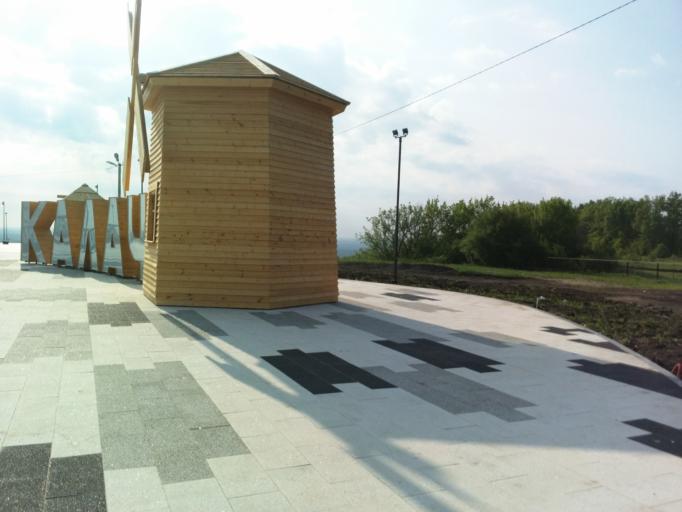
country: RU
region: Voronezj
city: Kalach
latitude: 50.4137
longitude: 41.0017
